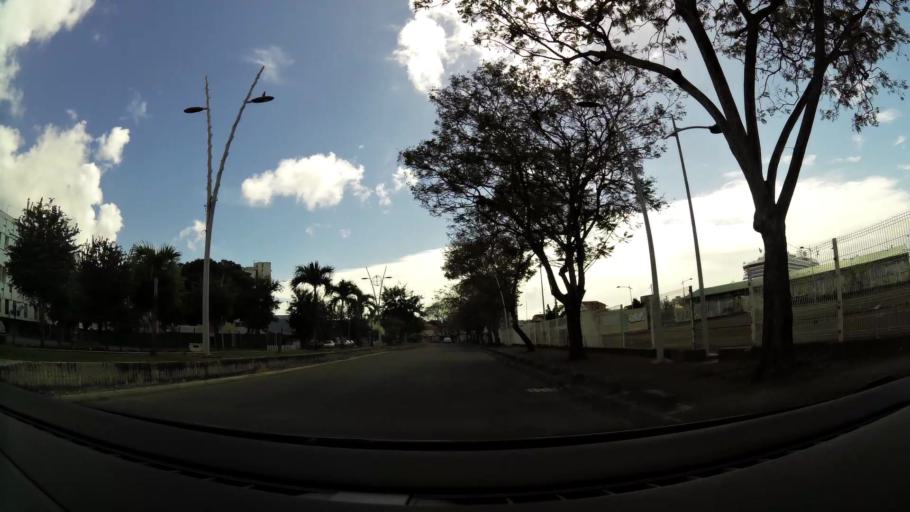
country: GP
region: Guadeloupe
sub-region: Guadeloupe
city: Pointe-a-Pitre
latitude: 16.2426
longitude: -61.5394
